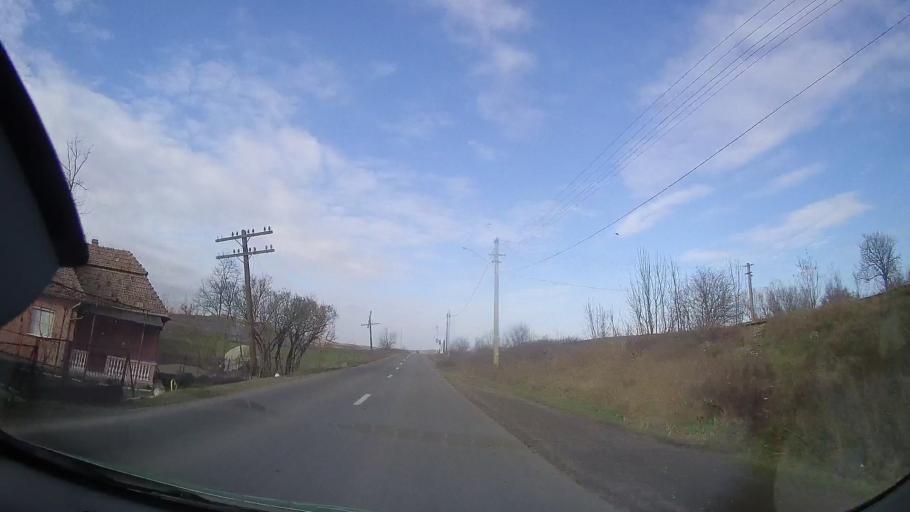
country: RO
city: Barza
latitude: 46.5668
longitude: 24.0931
